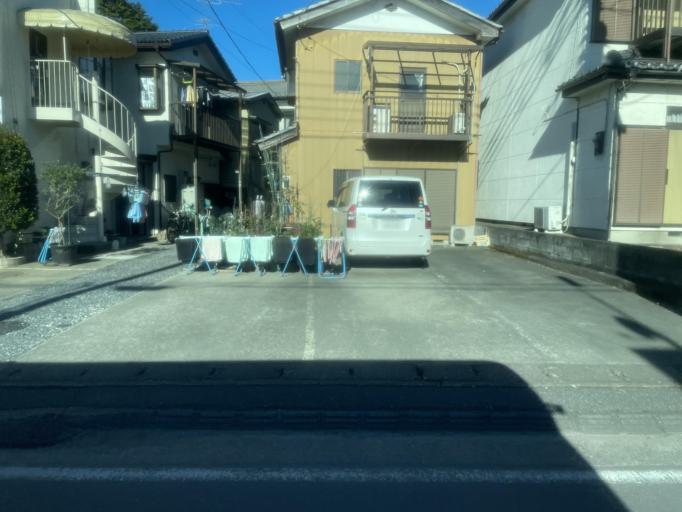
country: JP
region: Saitama
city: Ogawa
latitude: 36.0523
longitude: 139.2488
